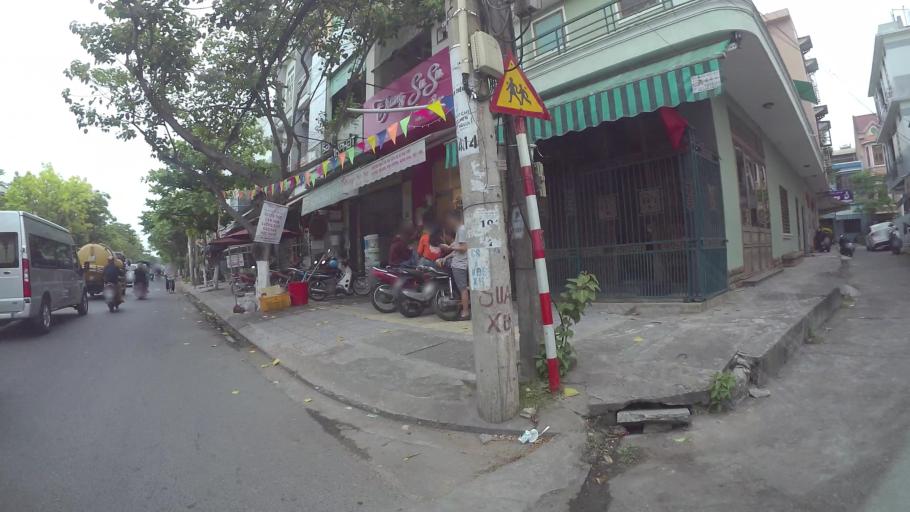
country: VN
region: Da Nang
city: Thanh Khe
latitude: 16.0636
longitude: 108.1920
